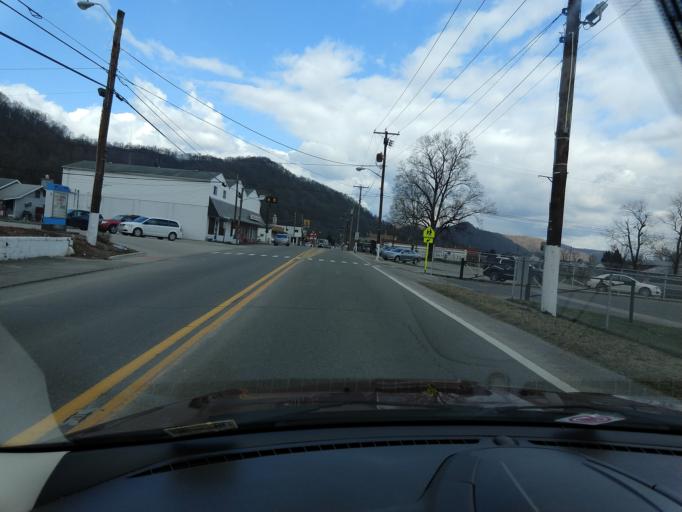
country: US
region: West Virginia
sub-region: Kanawha County
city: Marmet
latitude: 38.2456
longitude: -81.5671
